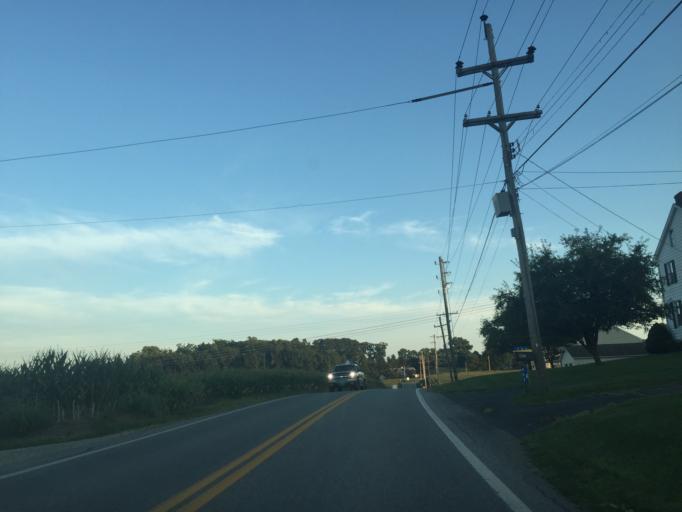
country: US
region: Pennsylvania
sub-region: York County
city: Susquehanna Trails
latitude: 39.7433
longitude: -76.3270
